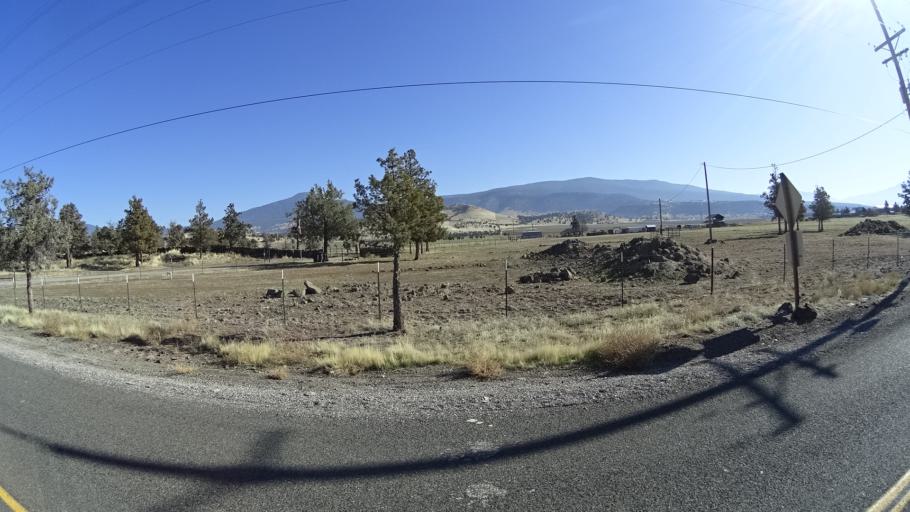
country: US
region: California
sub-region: Siskiyou County
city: Montague
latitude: 41.6700
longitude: -122.3697
